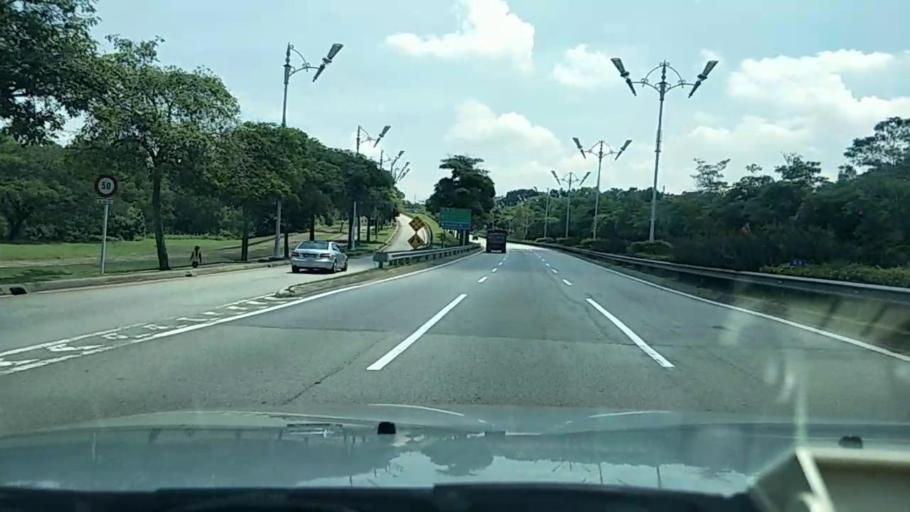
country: MY
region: Putrajaya
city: Putrajaya
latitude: 2.9554
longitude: 101.6928
